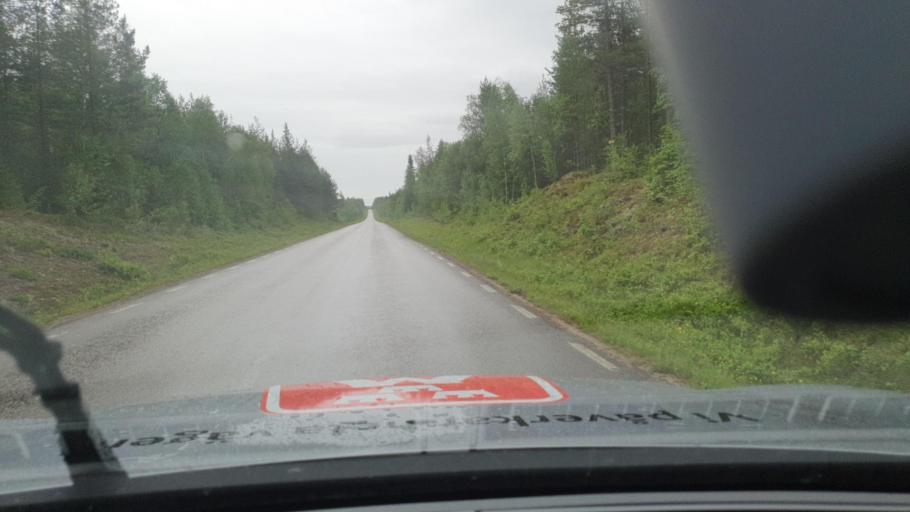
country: SE
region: Norrbotten
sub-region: Pajala Kommun
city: Pajala
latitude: 66.8368
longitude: 23.0932
